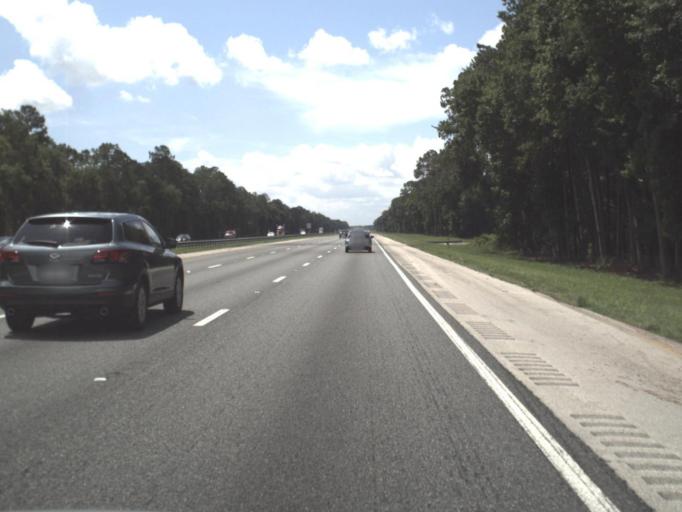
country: US
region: Florida
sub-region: Saint Johns County
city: Saint Augustine
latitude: 29.9482
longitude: -81.4373
